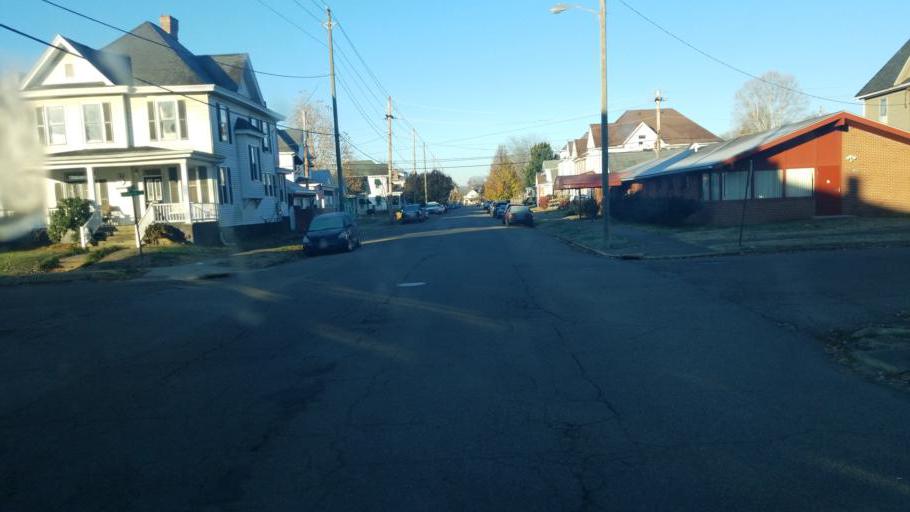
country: US
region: Ohio
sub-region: Scioto County
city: Portsmouth
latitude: 38.7425
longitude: -82.9796
